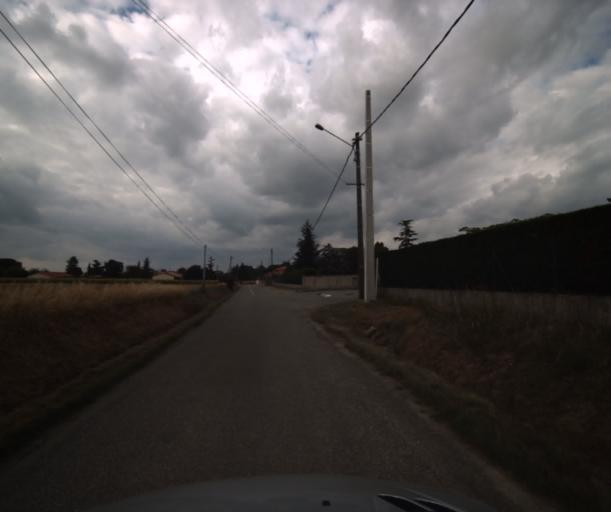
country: FR
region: Midi-Pyrenees
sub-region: Departement de la Haute-Garonne
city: Labarthe-sur-Leze
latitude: 43.4406
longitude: 1.3968
